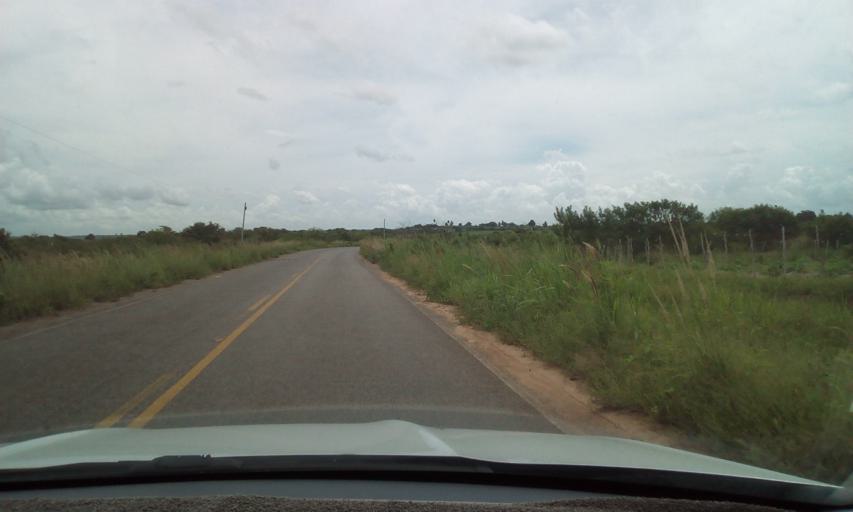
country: BR
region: Paraiba
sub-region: Mari
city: Mari
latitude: -7.1235
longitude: -35.3490
